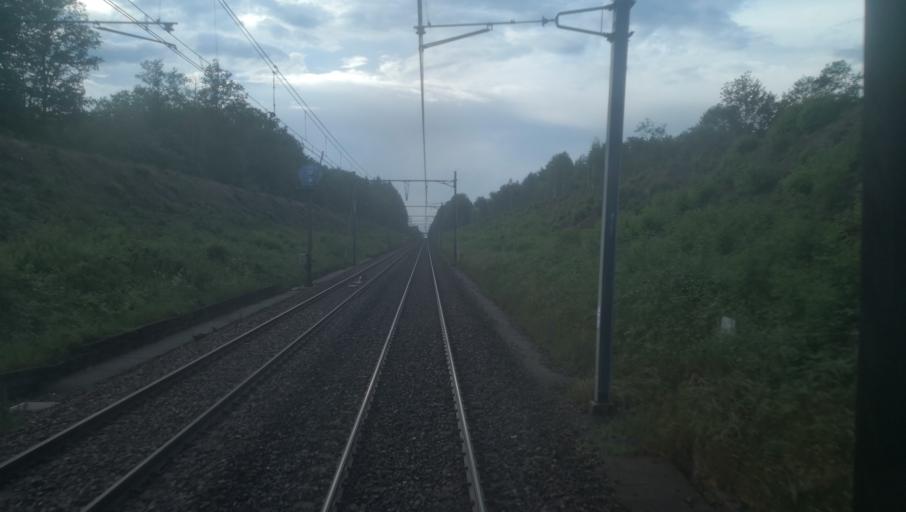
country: FR
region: Centre
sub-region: Departement du Loir-et-Cher
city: Lamotte-Beuvron
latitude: 47.6194
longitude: 2.0101
